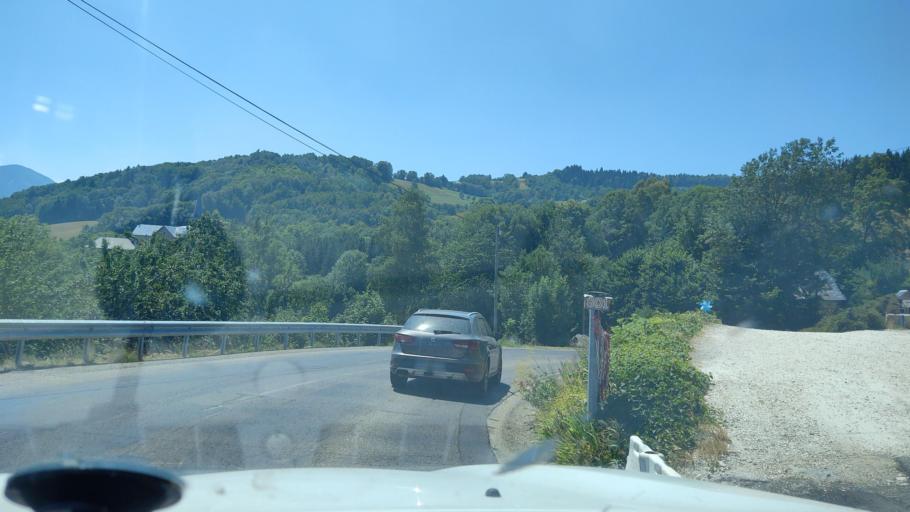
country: FR
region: Rhone-Alpes
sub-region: Departement de la Savoie
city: Barby
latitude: 45.6239
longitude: 6.0073
